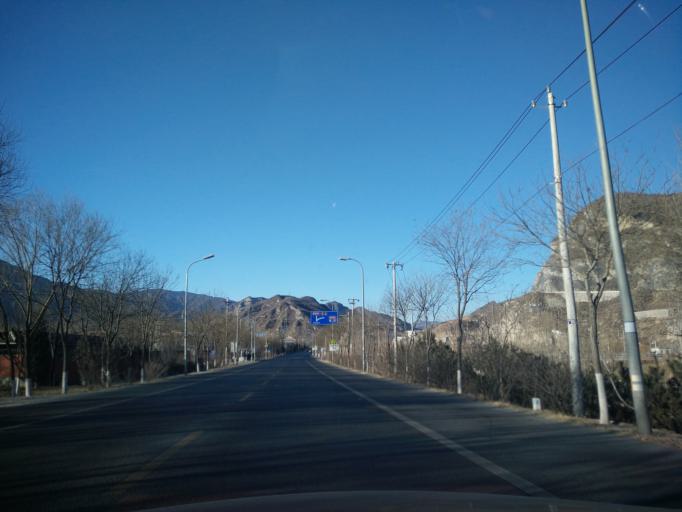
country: CN
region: Beijing
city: Miaofengshan
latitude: 39.9892
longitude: 116.0668
